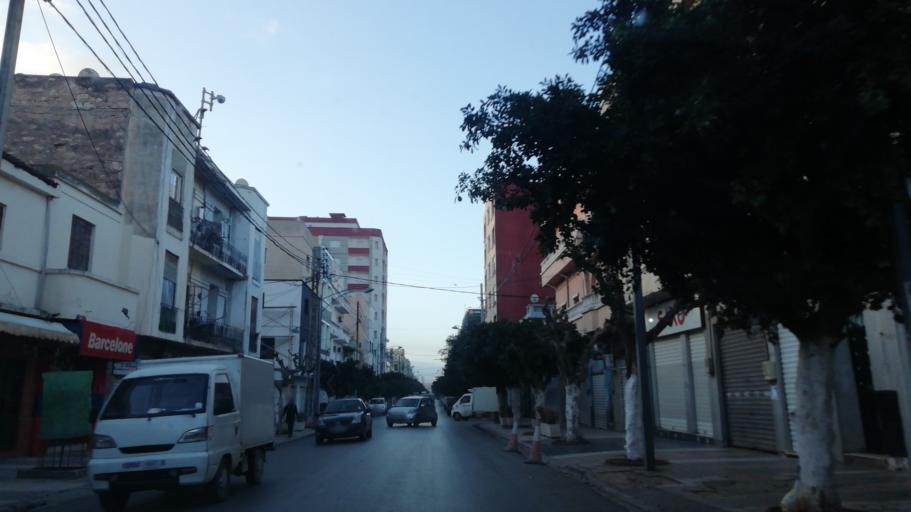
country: DZ
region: Oran
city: Oran
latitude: 35.6833
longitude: -0.6554
